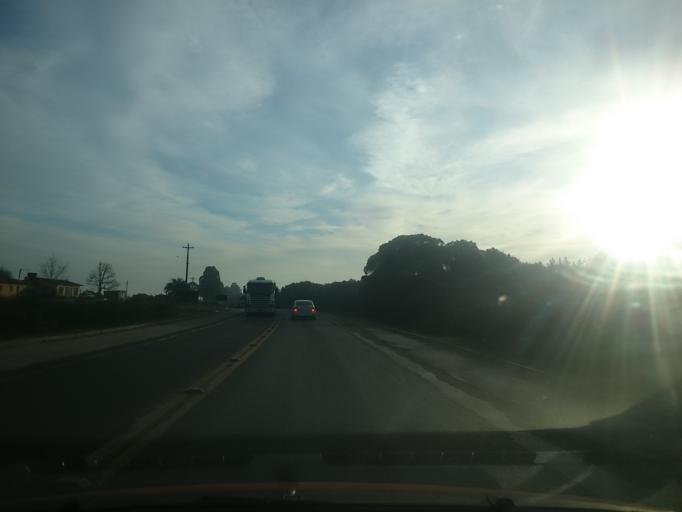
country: BR
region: Rio Grande do Sul
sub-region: Vacaria
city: Estrela
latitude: -28.2648
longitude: -50.7869
